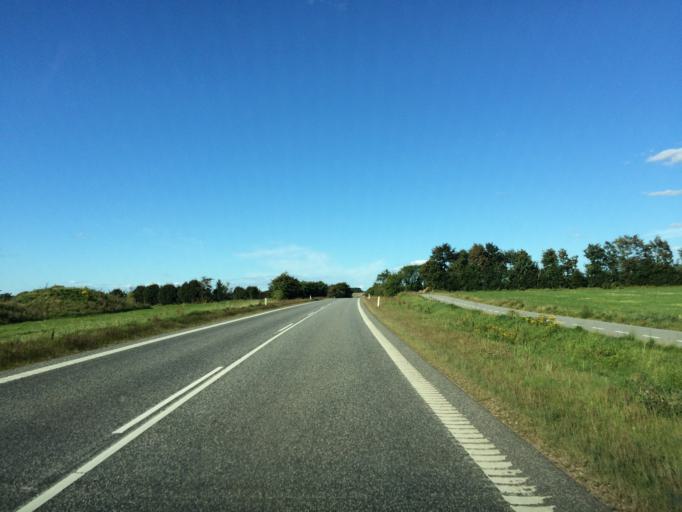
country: DK
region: Central Jutland
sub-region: Holstebro Kommune
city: Holstebro
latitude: 56.3099
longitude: 8.6043
